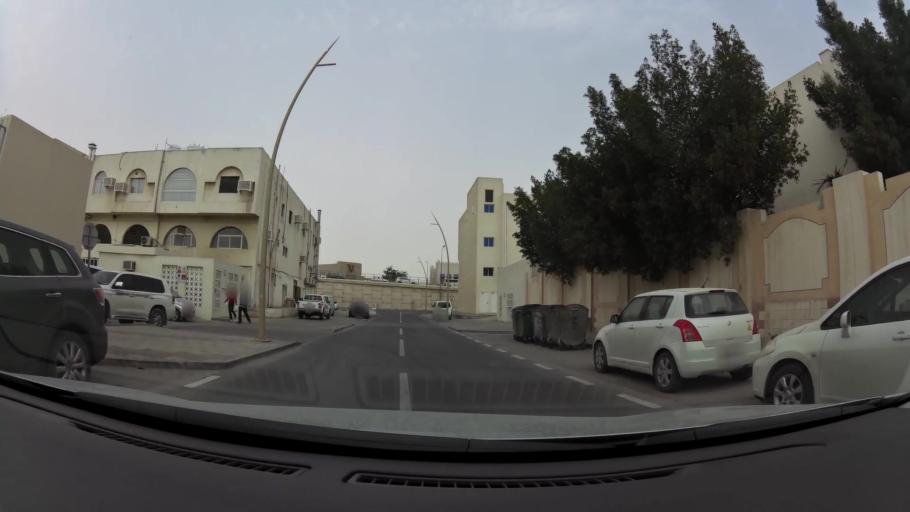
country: QA
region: Baladiyat ad Dawhah
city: Doha
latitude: 25.2643
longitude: 51.4994
